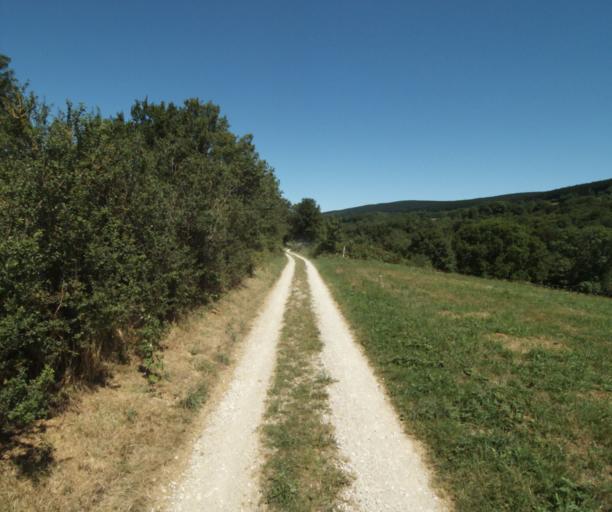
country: FR
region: Midi-Pyrenees
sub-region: Departement du Tarn
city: Dourgne
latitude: 43.4331
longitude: 2.1766
